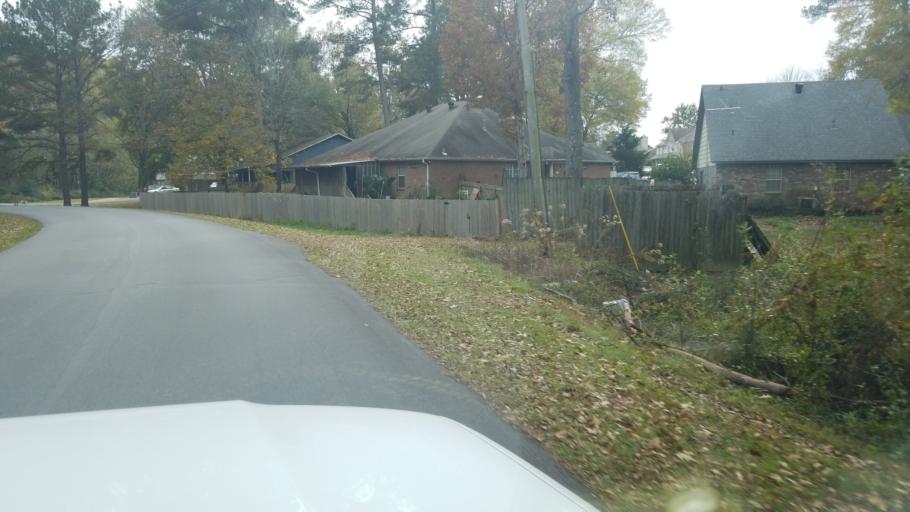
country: US
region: Mississippi
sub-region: Madison County
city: Ridgeland
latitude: 32.3829
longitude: -90.0330
